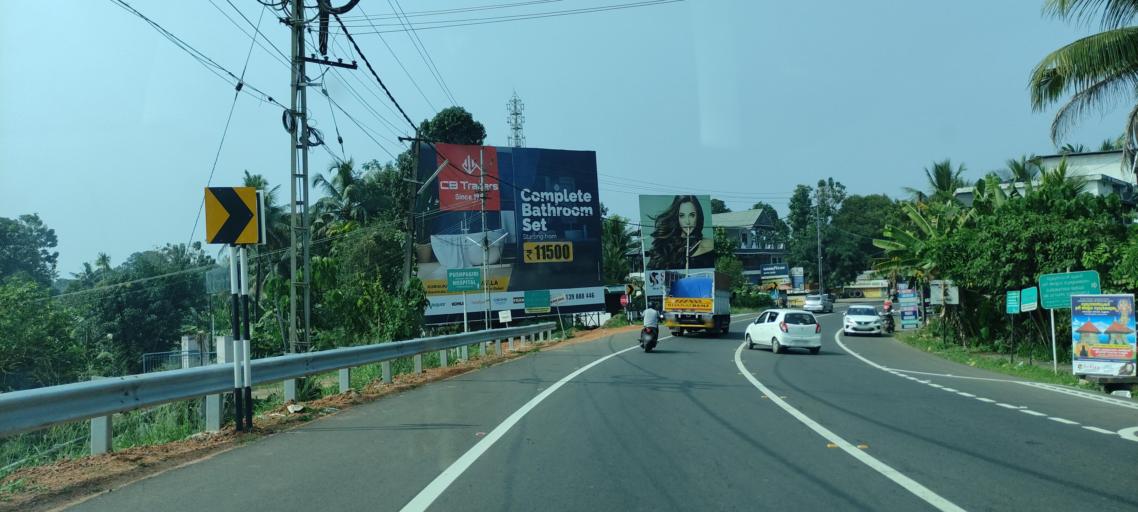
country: IN
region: Kerala
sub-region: Pattanamtitta
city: Adur
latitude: 9.2344
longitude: 76.6726
